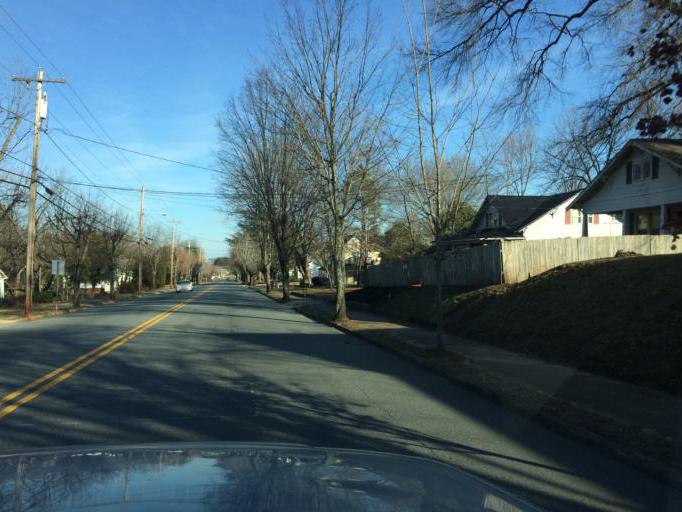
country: US
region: North Carolina
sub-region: Rutherford County
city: Forest City
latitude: 35.3322
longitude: -81.8566
